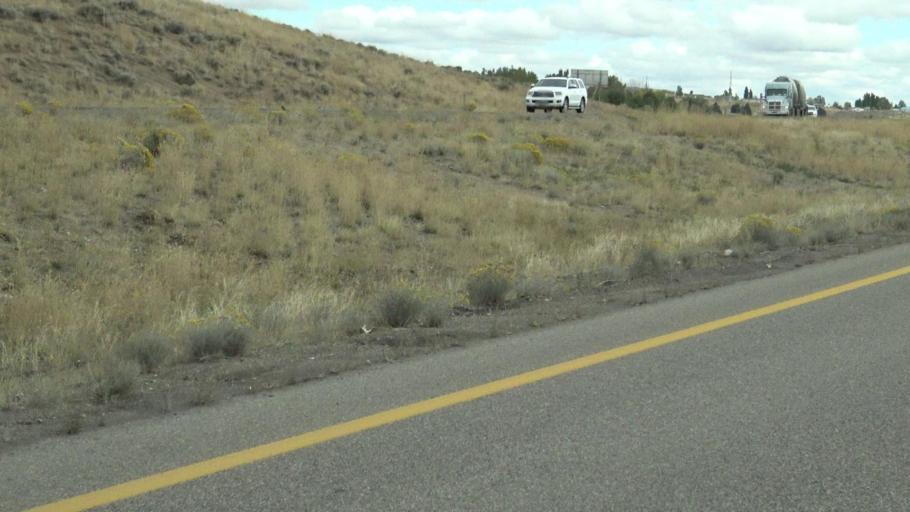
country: US
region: Nevada
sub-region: Elko County
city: Elko
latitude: 40.8376
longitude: -115.7807
